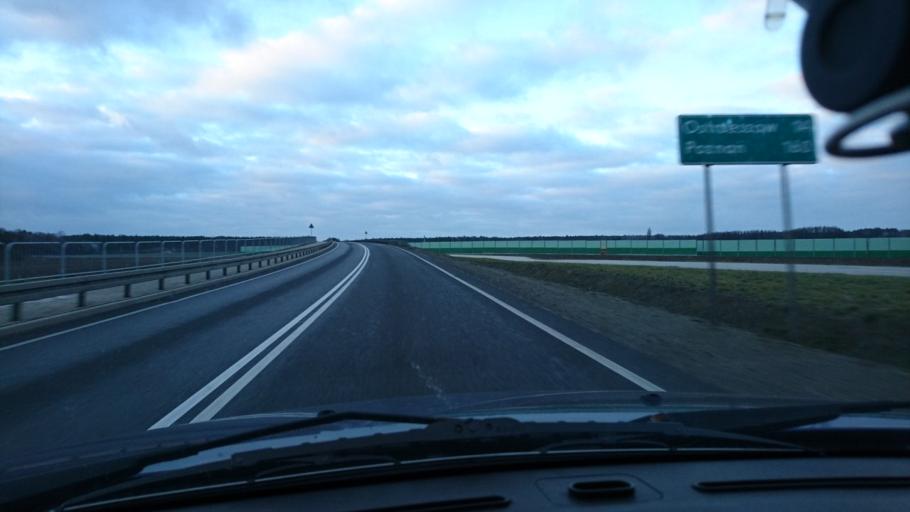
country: PL
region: Greater Poland Voivodeship
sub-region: Powiat kepinski
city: Kepno
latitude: 51.3156
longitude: 17.9818
